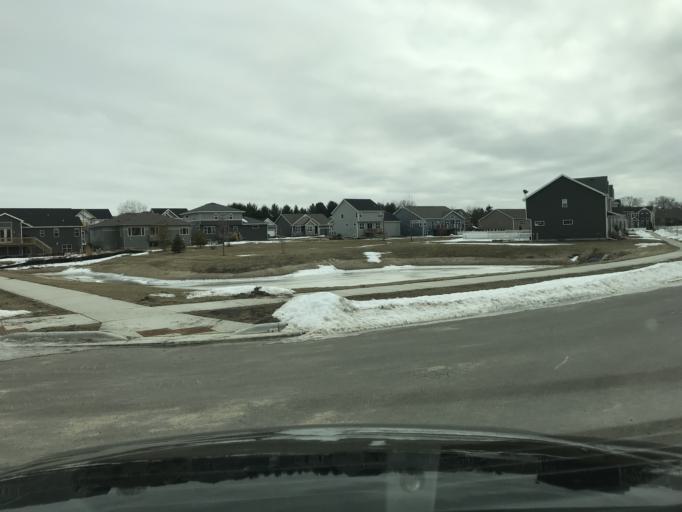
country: US
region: Wisconsin
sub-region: Dane County
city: Monona
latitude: 43.0942
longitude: -89.2741
